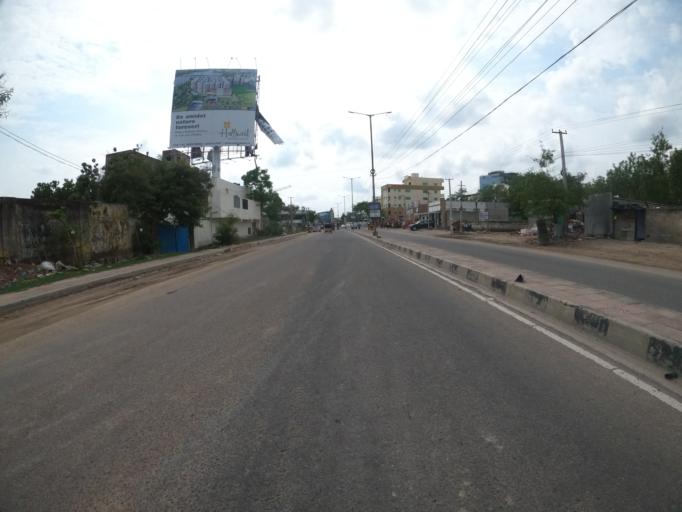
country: IN
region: Telangana
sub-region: Hyderabad
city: Hyderabad
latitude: 17.3832
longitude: 78.3637
